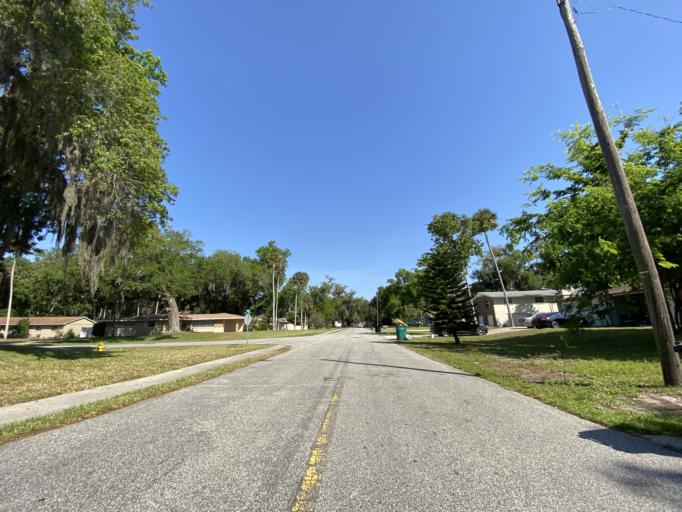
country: US
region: Florida
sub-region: Volusia County
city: South Daytona
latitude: 29.1654
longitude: -81.0128
